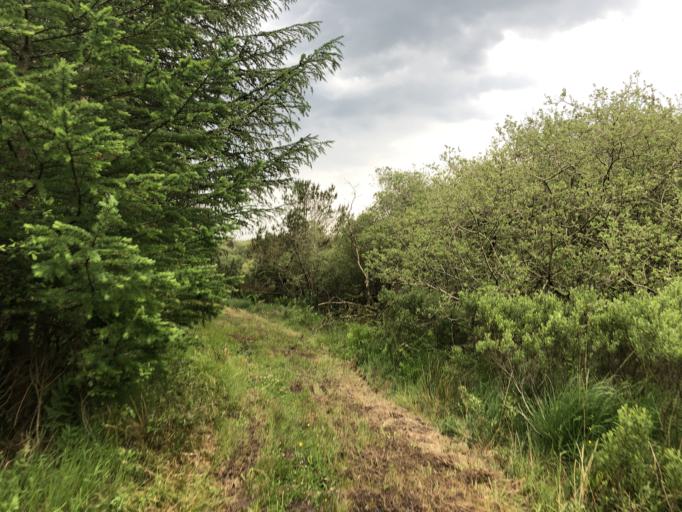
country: DK
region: Central Jutland
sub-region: Holstebro Kommune
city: Ulfborg
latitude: 56.2376
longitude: 8.4032
